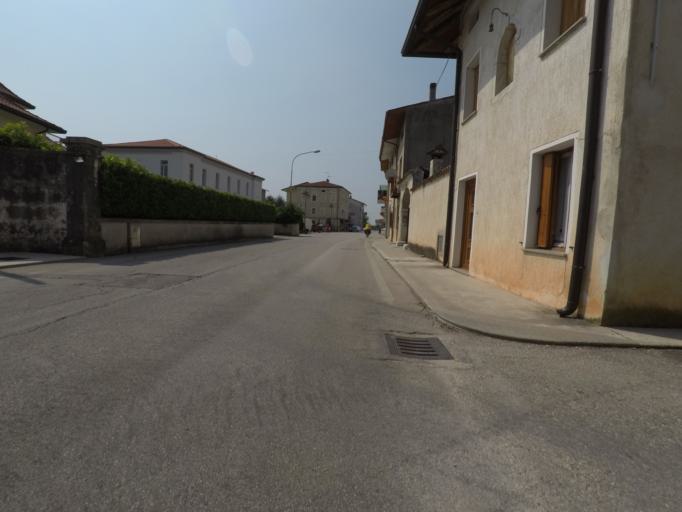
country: IT
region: Friuli Venezia Giulia
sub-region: Provincia di Pordenone
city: Montereale Valcellina
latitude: 46.1589
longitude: 12.6609
